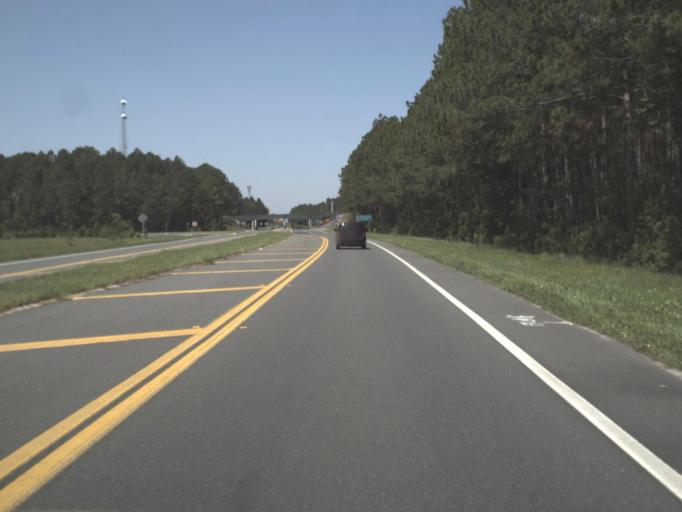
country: US
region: Florida
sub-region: Baker County
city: Macclenny
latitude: 30.2408
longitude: -82.2986
